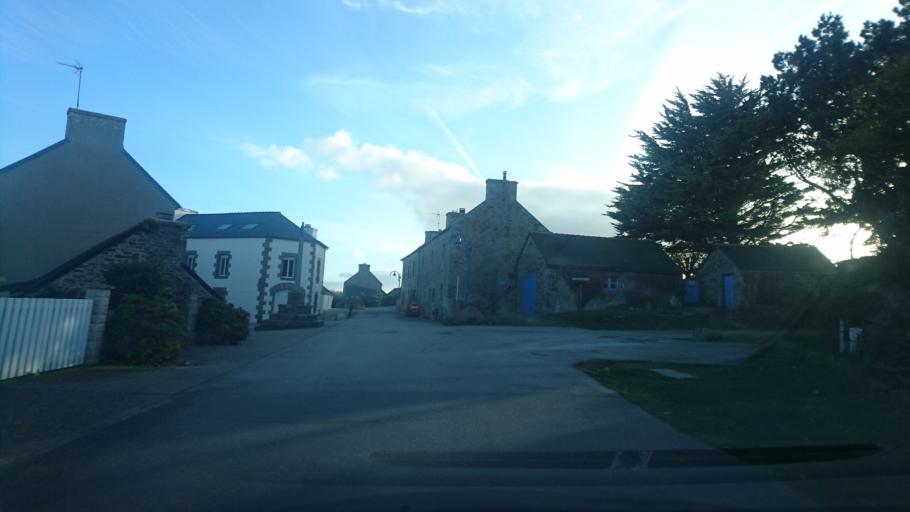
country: FR
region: Brittany
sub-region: Departement du Finistere
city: Lampaul-Plouarzel
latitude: 48.4247
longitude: -4.7694
